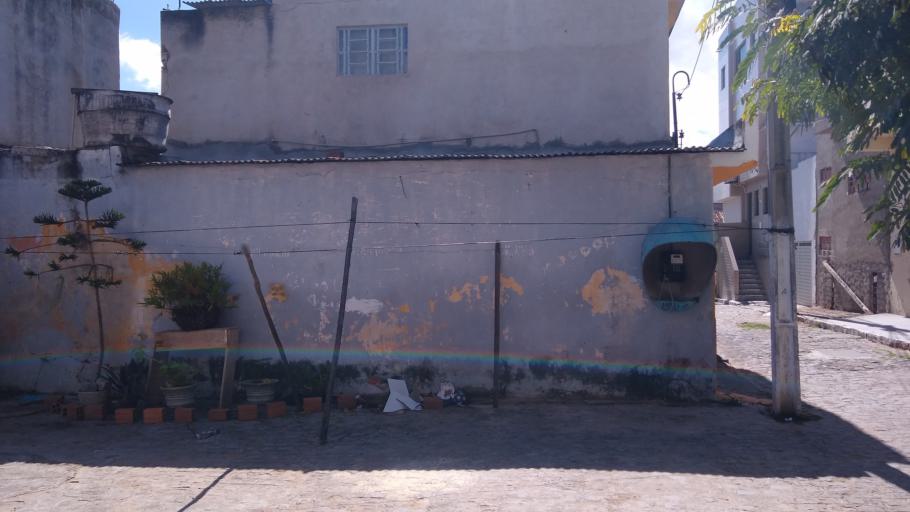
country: BR
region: Pernambuco
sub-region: Caruaru
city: Caruaru
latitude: -8.2788
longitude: -35.9779
